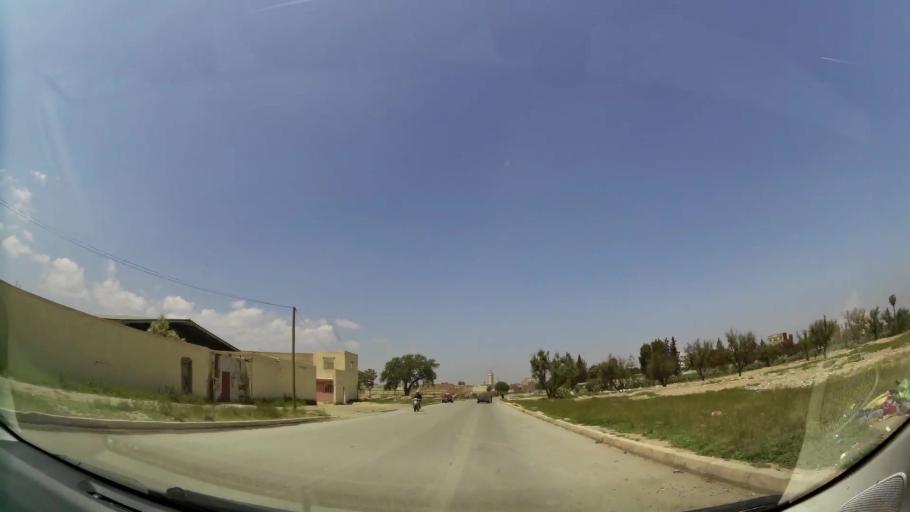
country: MA
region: Oriental
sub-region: Oujda-Angad
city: Oujda
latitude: 34.6895
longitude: -1.8975
